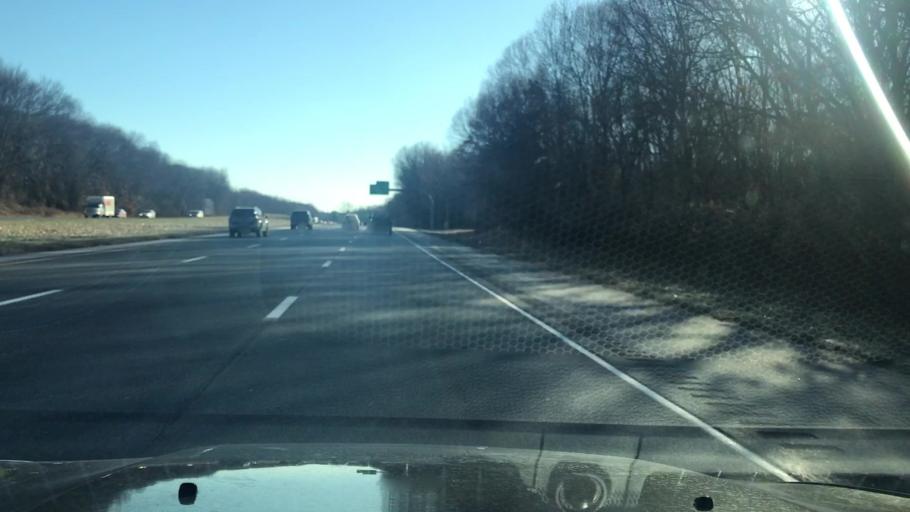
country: US
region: Connecticut
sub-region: Hartford County
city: Bristol
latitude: 41.6047
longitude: -72.9021
